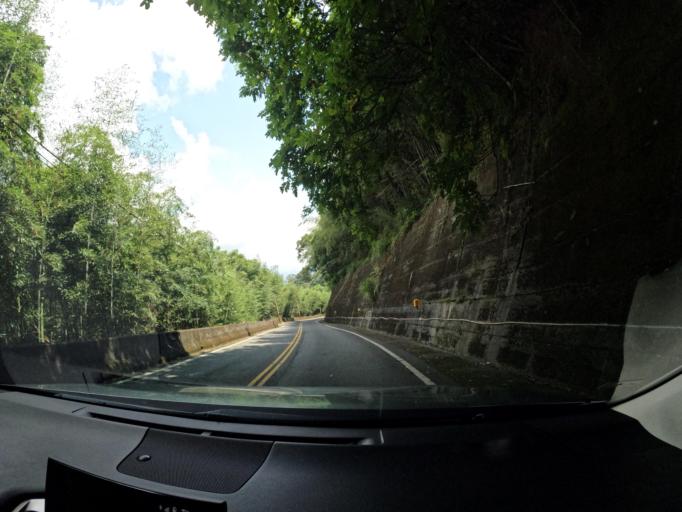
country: TW
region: Taiwan
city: Fengyuan
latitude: 24.3828
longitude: 120.8246
